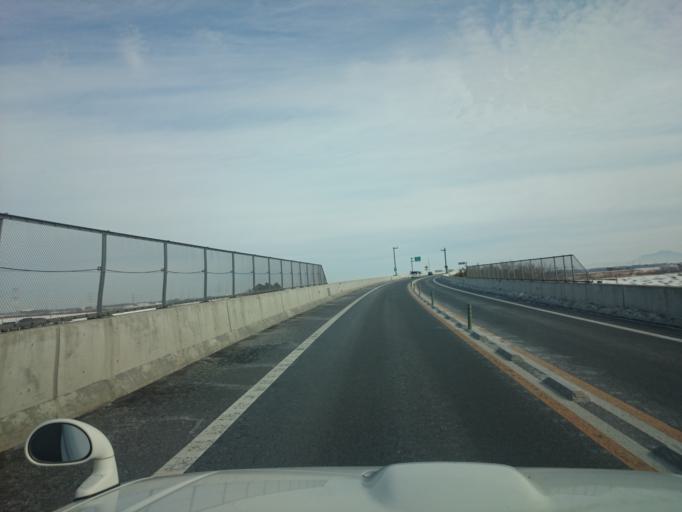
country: JP
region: Ibaraki
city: Sakai
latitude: 36.1113
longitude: 139.7592
